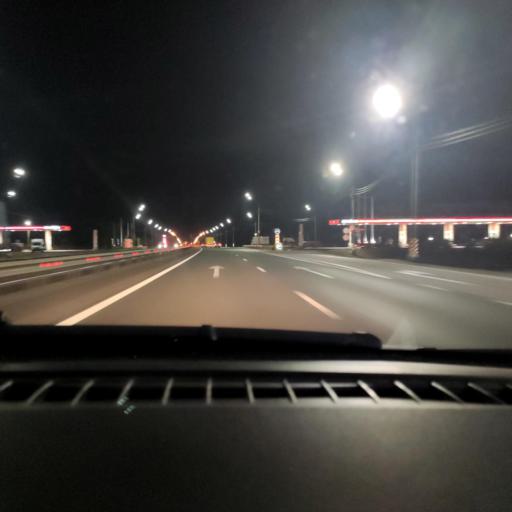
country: RU
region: Lipetsk
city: Khlevnoye
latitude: 52.2187
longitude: 39.1341
